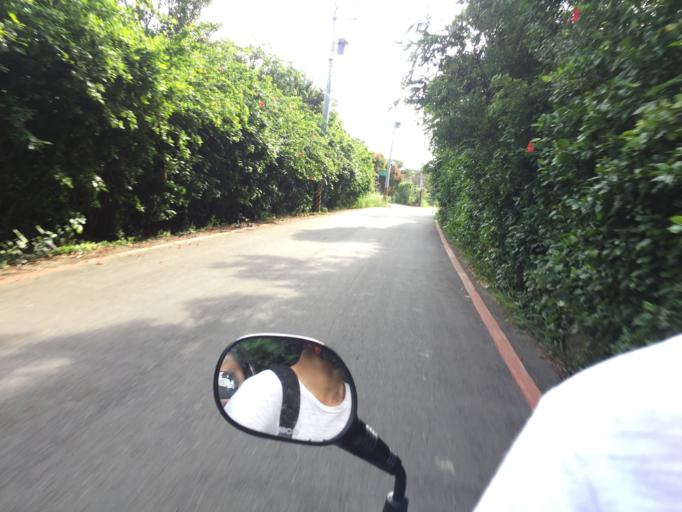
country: TW
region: Taiwan
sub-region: Hsinchu
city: Hsinchu
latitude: 24.7753
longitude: 120.9257
